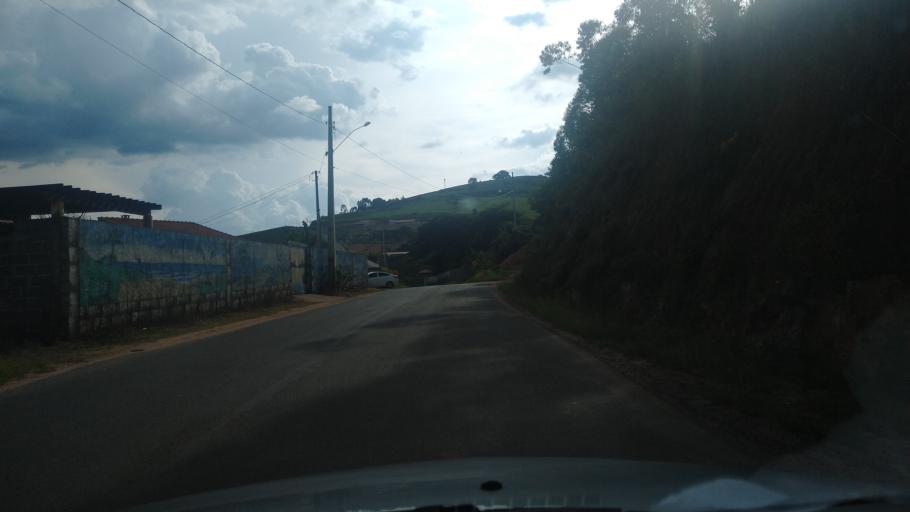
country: BR
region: Minas Gerais
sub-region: Extrema
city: Extrema
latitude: -22.7317
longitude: -46.3622
